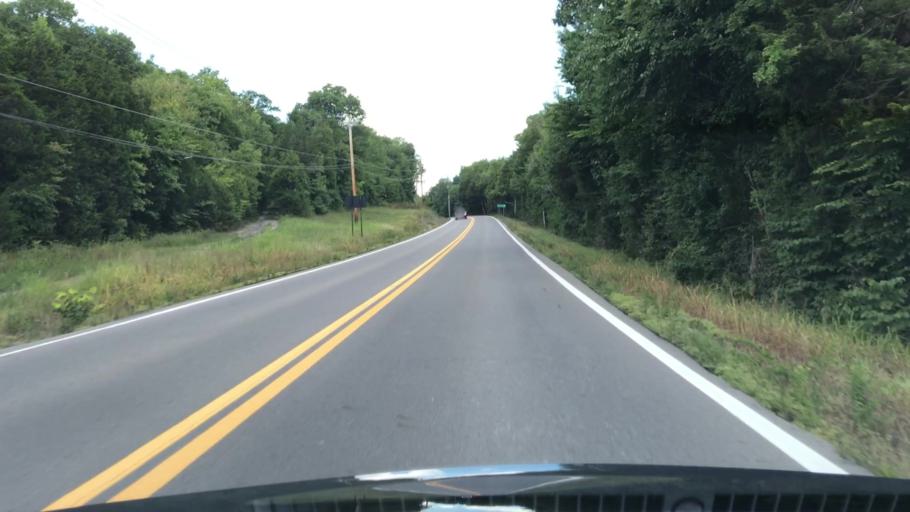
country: US
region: Tennessee
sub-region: Williamson County
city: Nolensville
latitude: 35.8512
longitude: -86.5986
